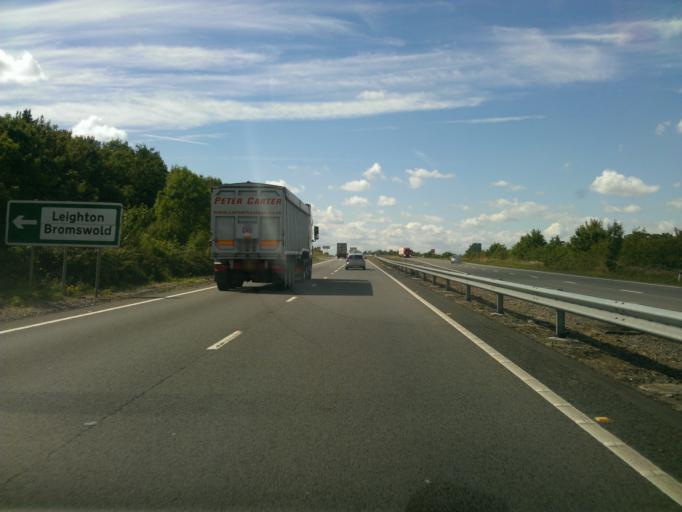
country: GB
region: England
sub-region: Bedford
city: Pertenhall
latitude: 52.3512
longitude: -0.3727
